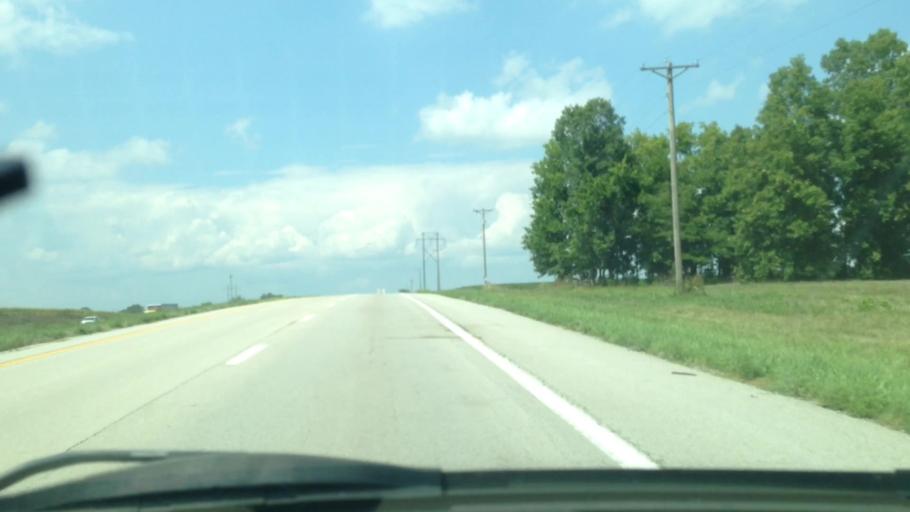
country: US
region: Missouri
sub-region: Lincoln County
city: Troy
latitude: 39.1475
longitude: -90.9687
